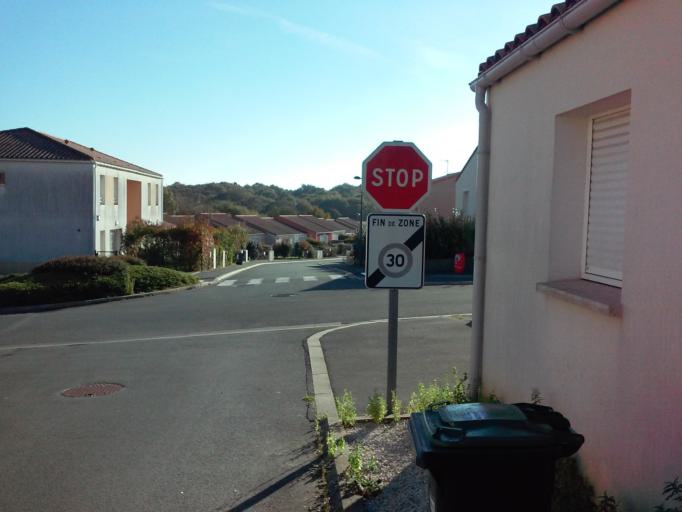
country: FR
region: Pays de la Loire
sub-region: Departement de la Vendee
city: La Roche-sur-Yon
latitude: 46.6667
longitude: -1.3943
